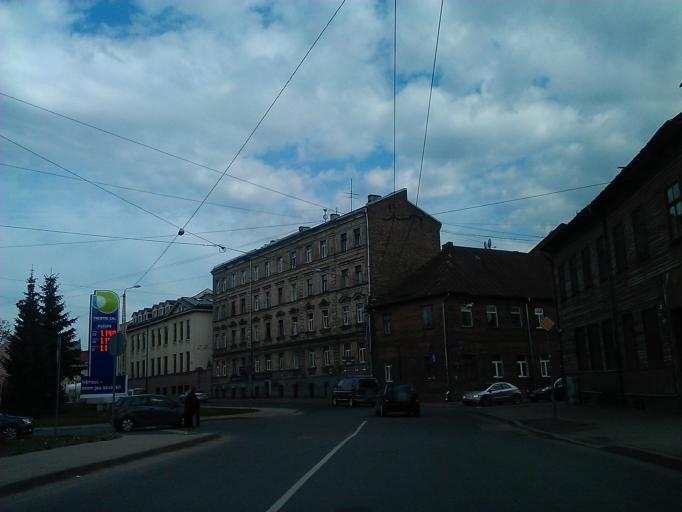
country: LV
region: Riga
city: Riga
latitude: 56.9407
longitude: 24.1367
